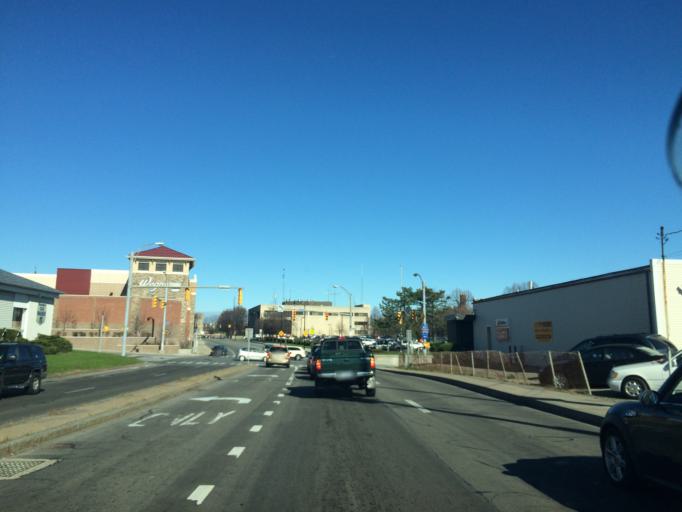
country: US
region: New York
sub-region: Monroe County
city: Brighton
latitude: 43.1461
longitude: -77.5540
